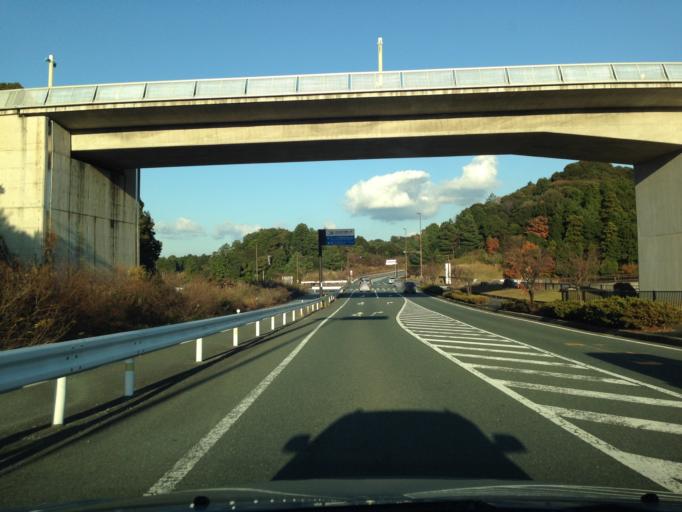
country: JP
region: Shizuoka
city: Fukuroi
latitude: 34.7451
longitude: 137.9648
